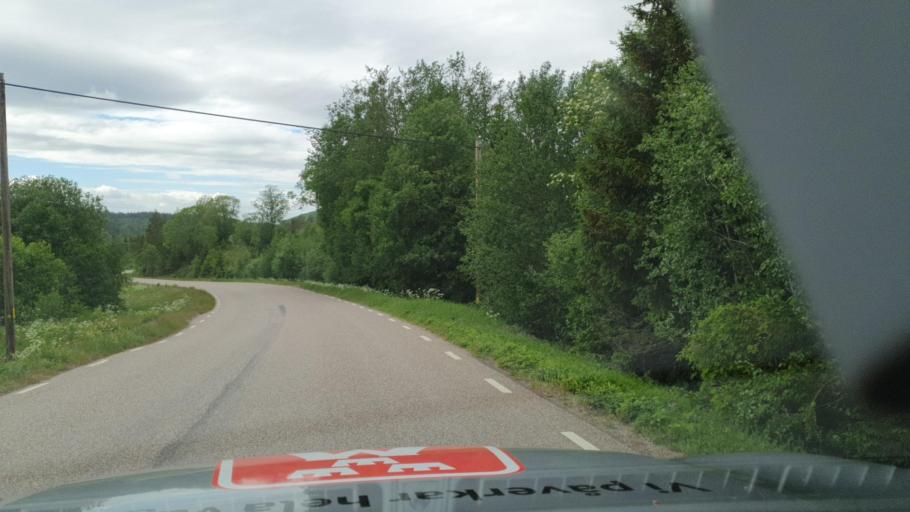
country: SE
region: Vaesternorrland
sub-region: Kramfors Kommun
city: Nordingra
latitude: 62.8788
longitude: 18.4149
